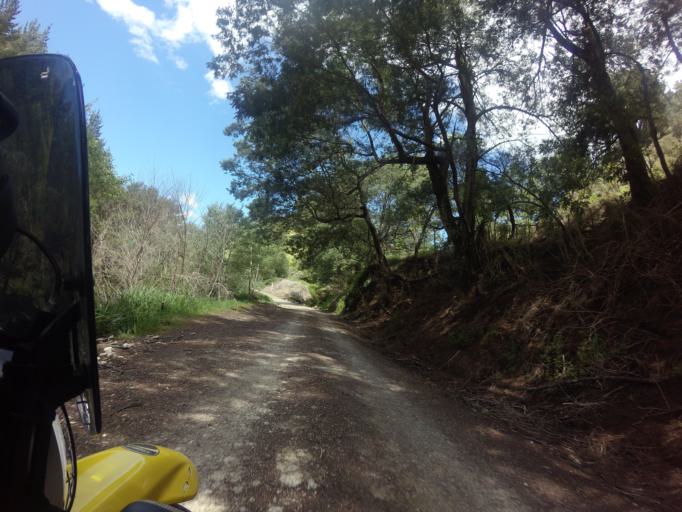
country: NZ
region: Hawke's Bay
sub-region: Wairoa District
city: Wairoa
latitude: -38.9712
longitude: 177.6714
